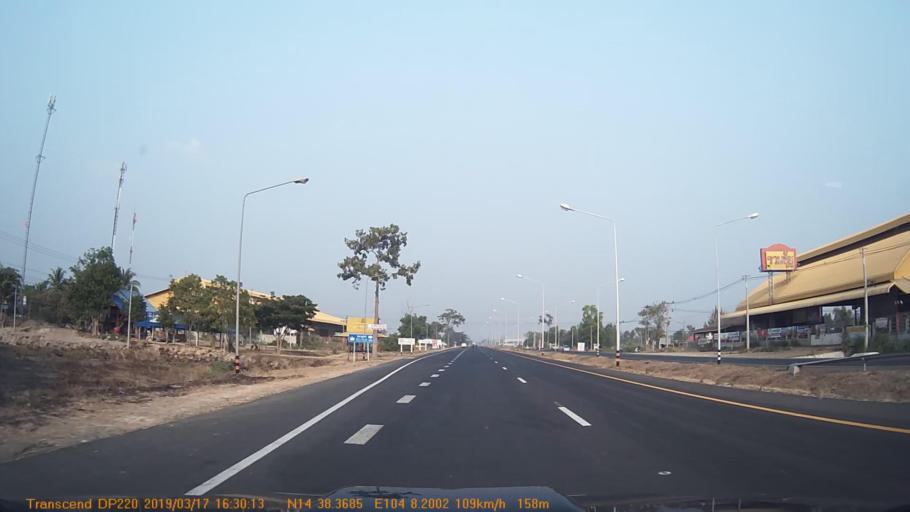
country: TH
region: Sisaket
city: Phu Sing
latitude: 14.6395
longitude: 104.1371
